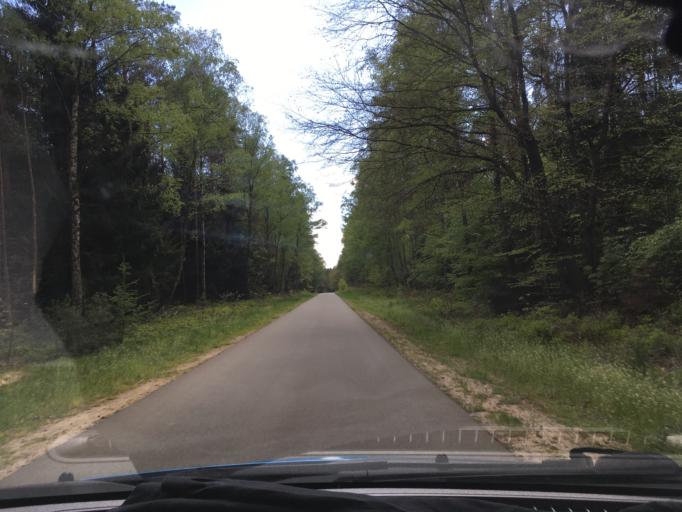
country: DE
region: Lower Saxony
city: Stoetze
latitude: 53.1154
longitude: 10.7893
